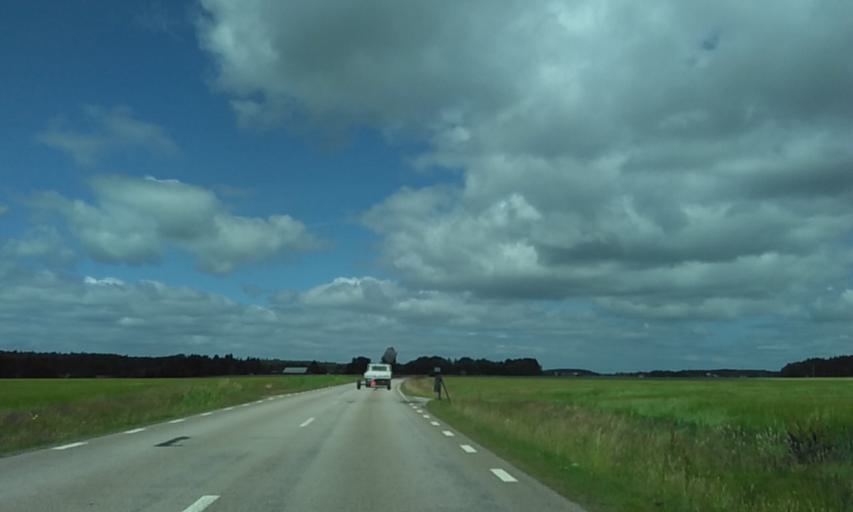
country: SE
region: Vaestra Goetaland
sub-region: Grastorps Kommun
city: Graestorp
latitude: 58.2844
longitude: 12.6726
